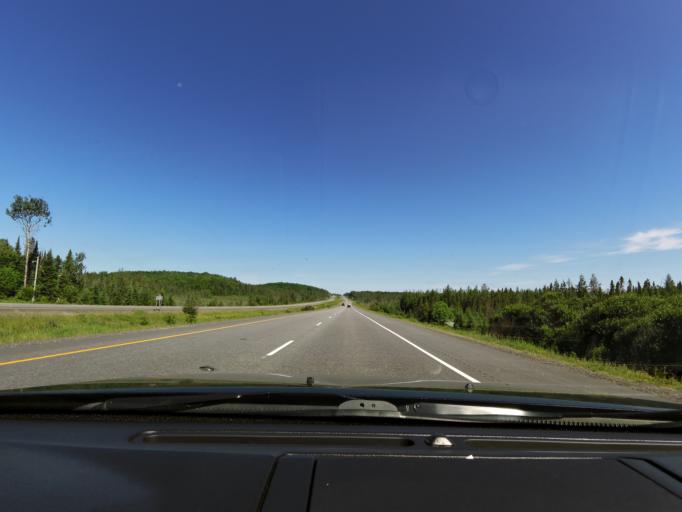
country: CA
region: Ontario
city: Huntsville
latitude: 45.4727
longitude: -79.2689
